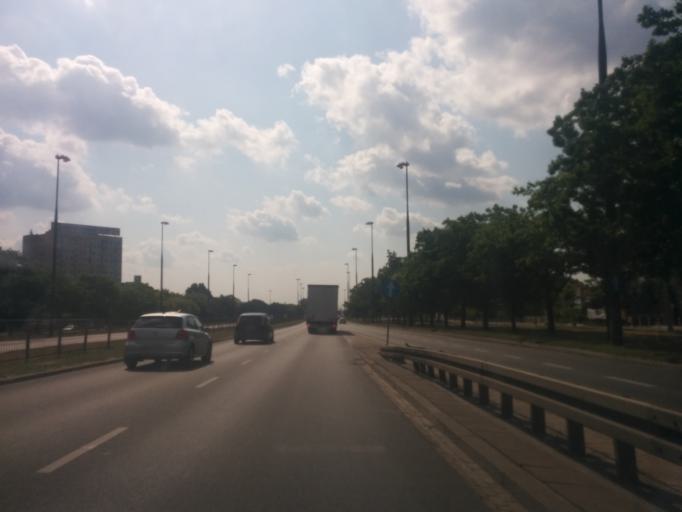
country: PL
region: Masovian Voivodeship
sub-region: Warszawa
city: Bialoleka
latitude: 52.3064
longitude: 20.9853
